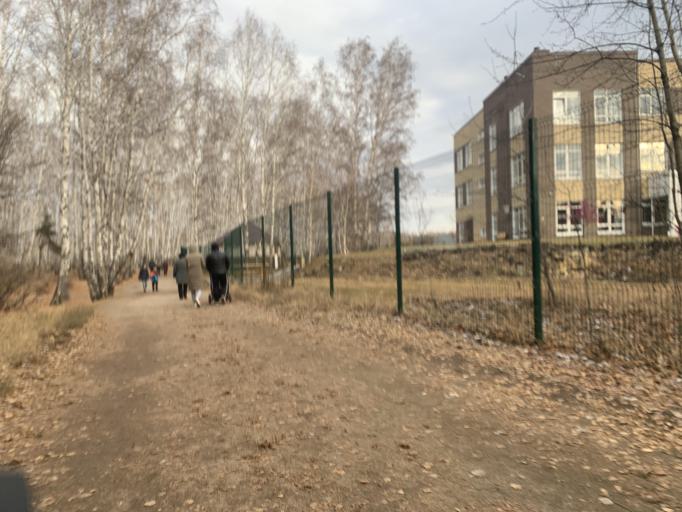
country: RU
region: Chelyabinsk
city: Roshchino
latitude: 55.1997
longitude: 61.3021
